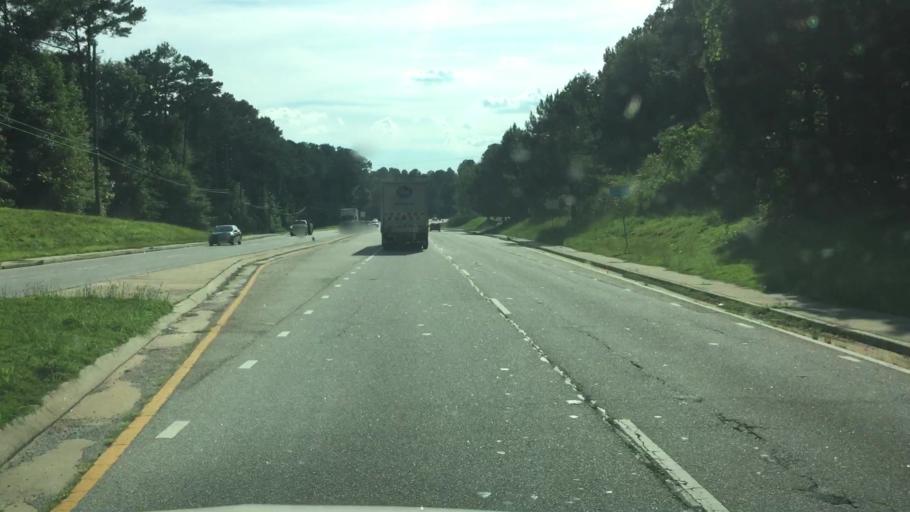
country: US
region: Georgia
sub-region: Rockdale County
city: Lakeview Estates
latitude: 33.7725
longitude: -84.0609
